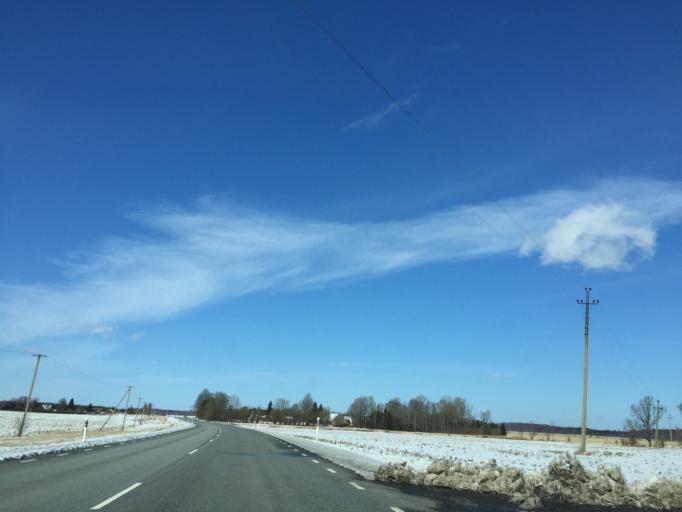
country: EE
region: Paernumaa
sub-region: Audru vald
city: Audru
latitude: 58.4585
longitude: 24.2236
